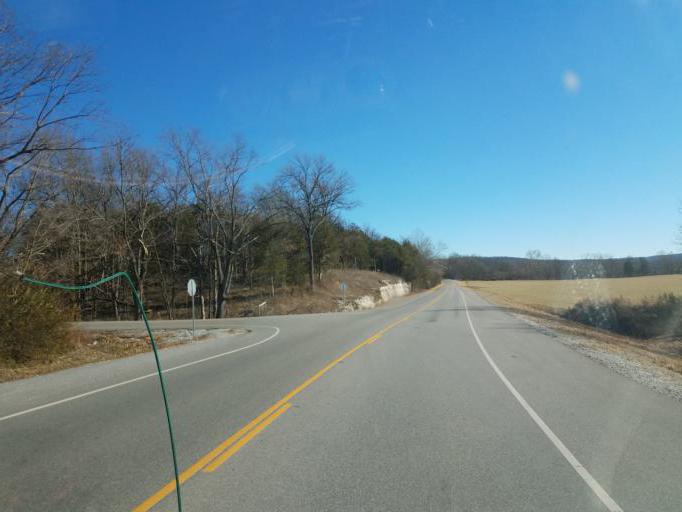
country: US
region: Arkansas
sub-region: Washington County
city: Elkins
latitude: 36.0304
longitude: -94.0167
